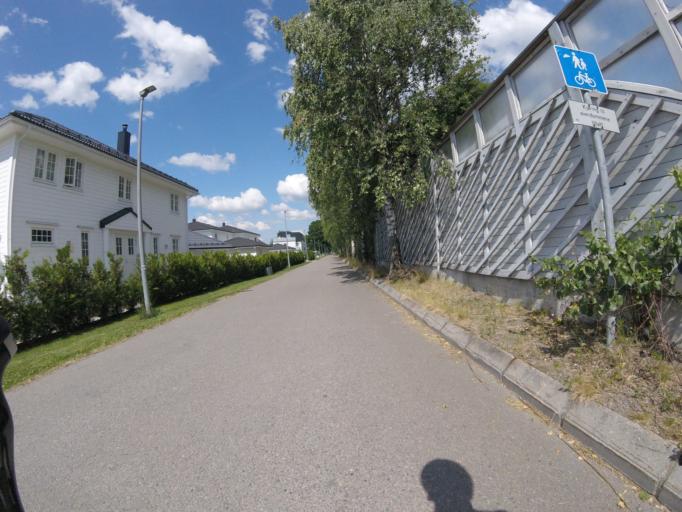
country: NO
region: Akershus
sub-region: Skedsmo
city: Lillestrom
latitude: 59.9568
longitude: 11.0709
